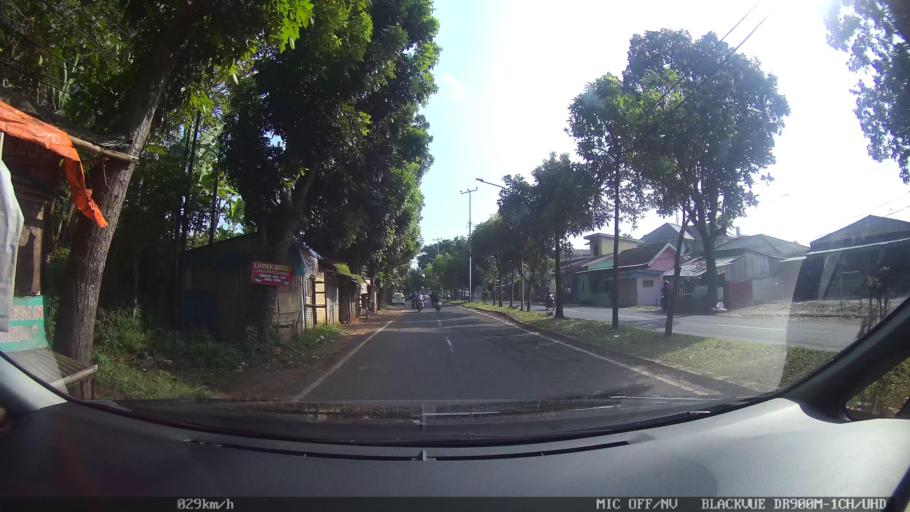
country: ID
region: Lampung
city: Bandarlampung
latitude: -5.4243
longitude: 105.2468
